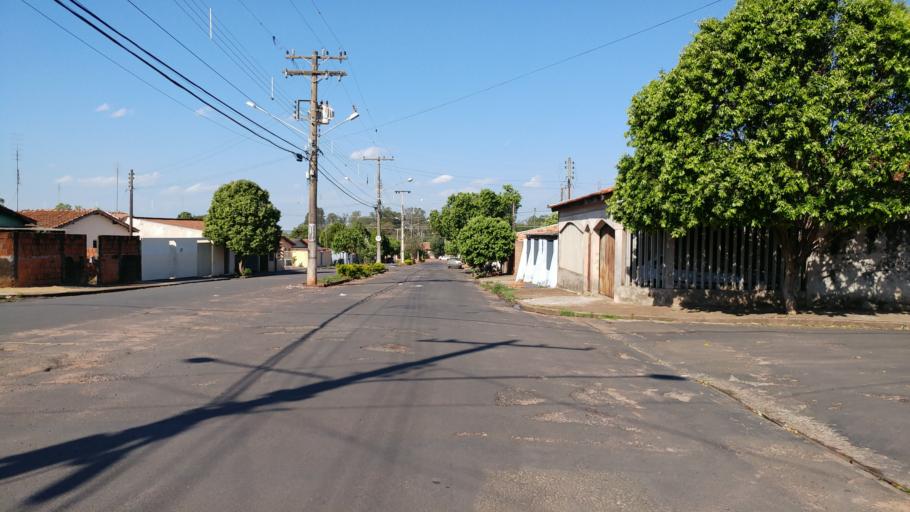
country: BR
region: Sao Paulo
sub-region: Paraguacu Paulista
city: Paraguacu Paulista
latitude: -22.4271
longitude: -50.5734
